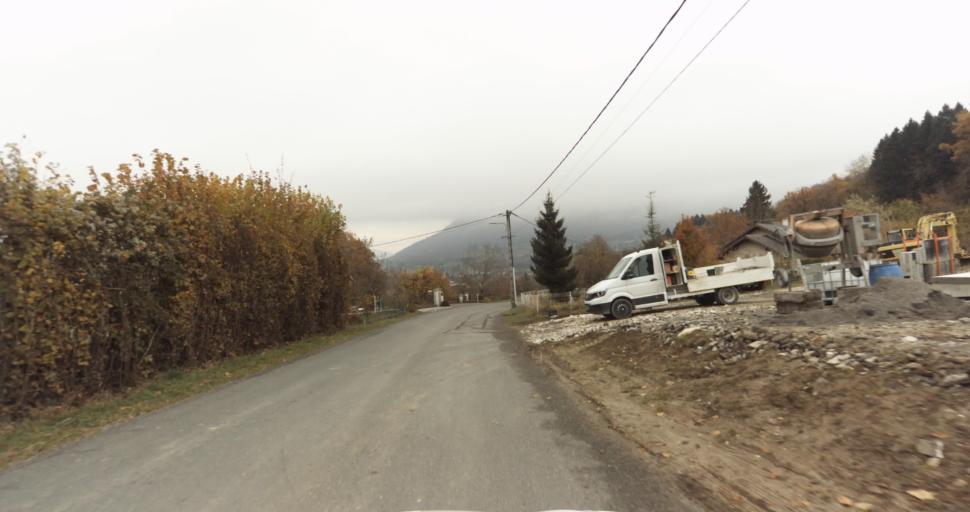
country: FR
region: Rhone-Alpes
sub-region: Departement de la Haute-Savoie
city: Cusy
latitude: 45.7741
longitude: 6.0136
